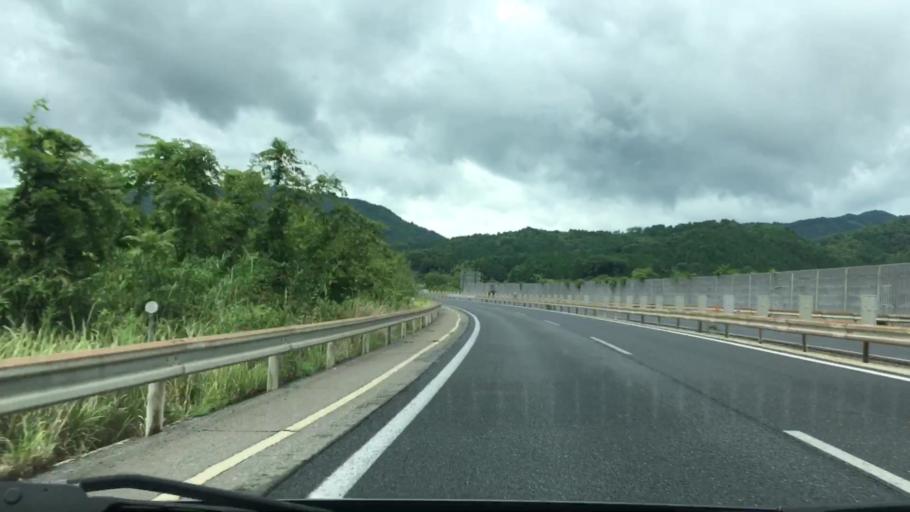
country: JP
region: Okayama
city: Takahashi
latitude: 34.9901
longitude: 133.7009
